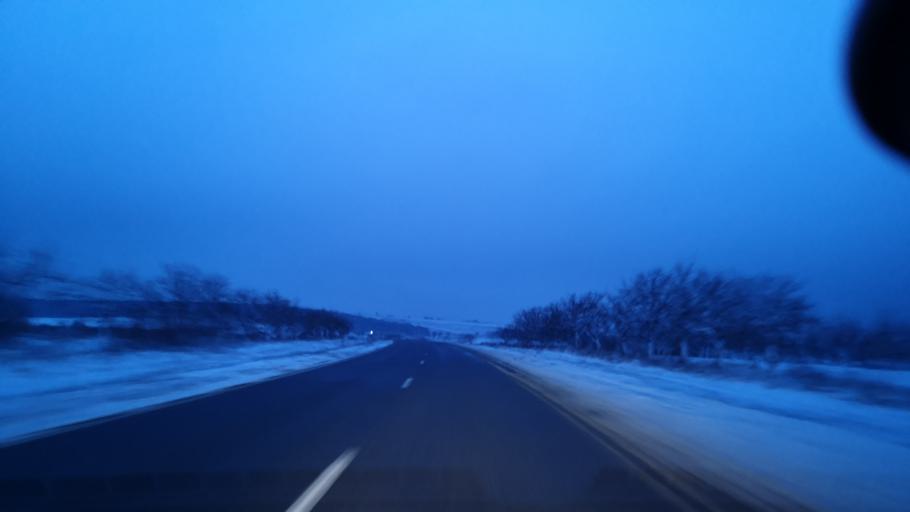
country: MD
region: Rezina
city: Saharna
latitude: 47.6094
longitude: 28.8305
